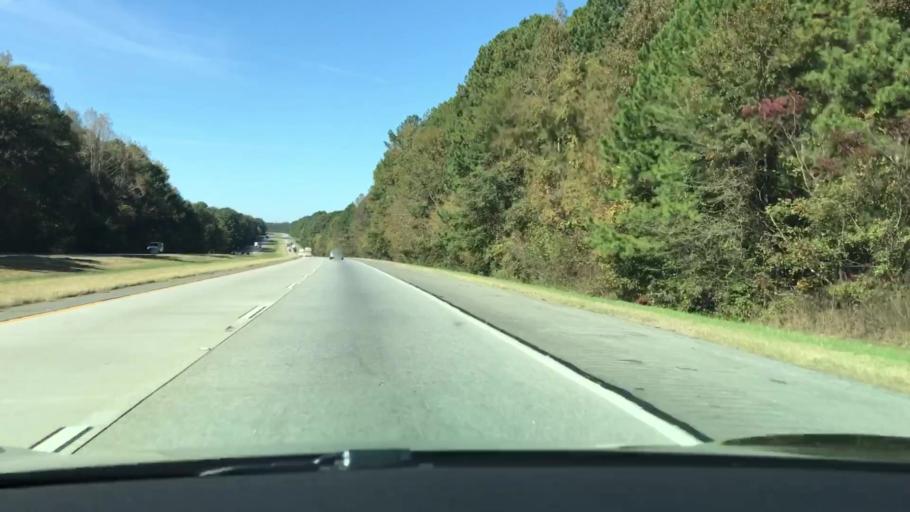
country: US
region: Georgia
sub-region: Greene County
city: Union Point
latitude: 33.5469
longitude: -83.0337
